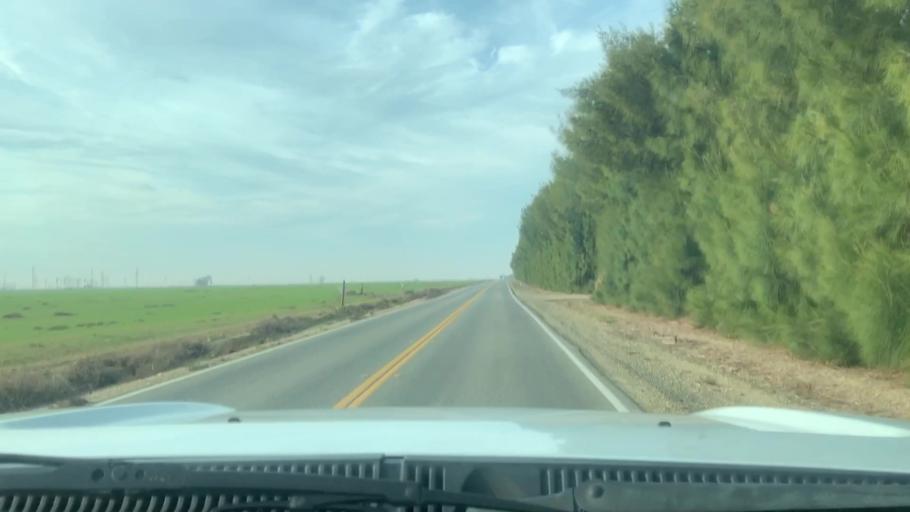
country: US
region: California
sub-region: Kern County
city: Lost Hills
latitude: 35.5129
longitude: -119.7498
